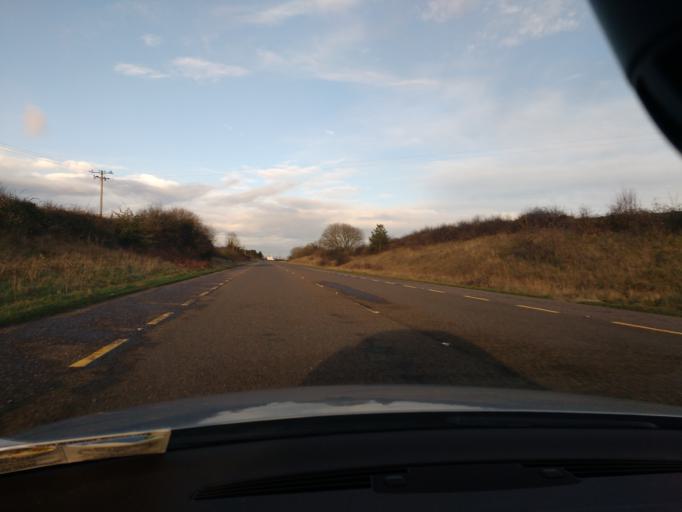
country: IE
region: Munster
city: Thurles
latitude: 52.6800
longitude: -7.6693
